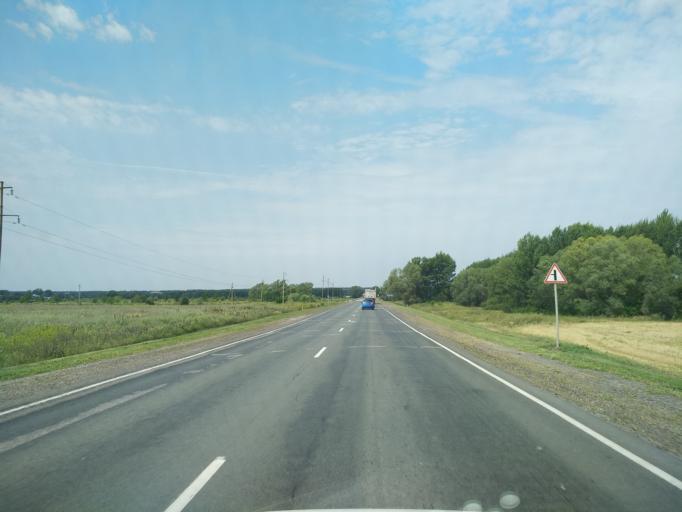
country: RU
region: Voronezj
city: Orlovo
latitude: 51.6802
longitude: 39.6145
